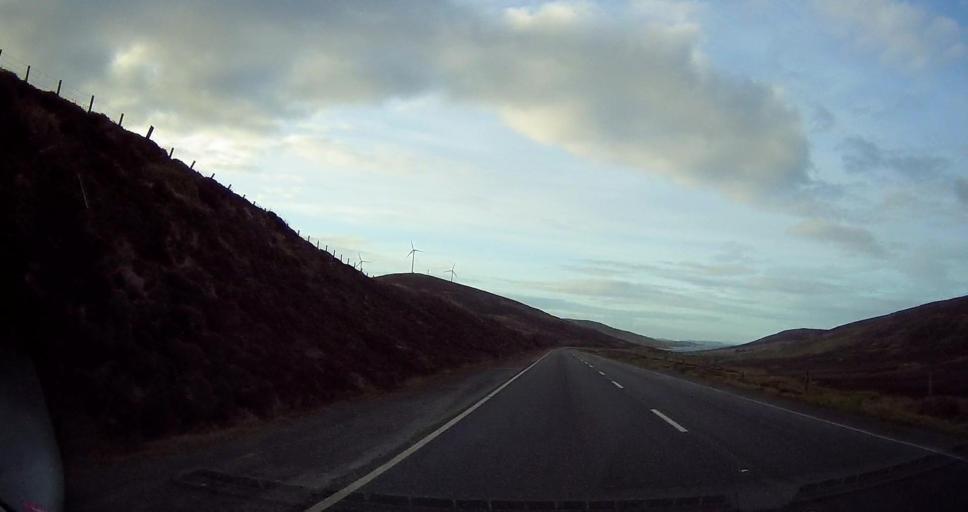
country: GB
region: Scotland
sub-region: Shetland Islands
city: Lerwick
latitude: 60.1508
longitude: -1.2374
